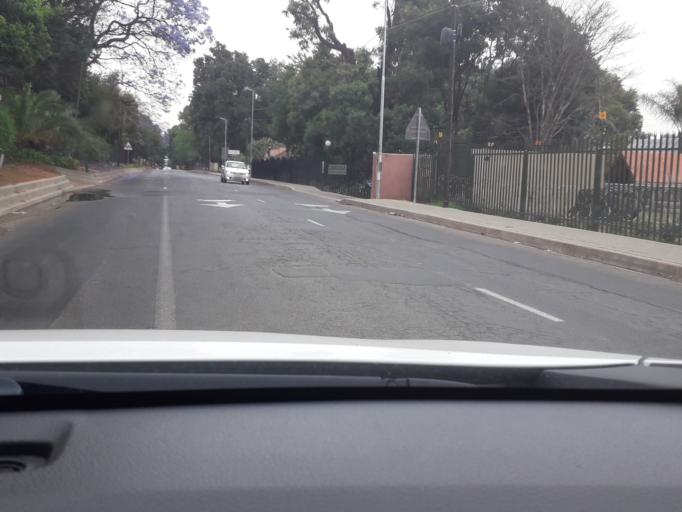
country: ZA
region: Gauteng
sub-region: City of Johannesburg Metropolitan Municipality
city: Johannesburg
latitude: -26.1029
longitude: 28.0625
